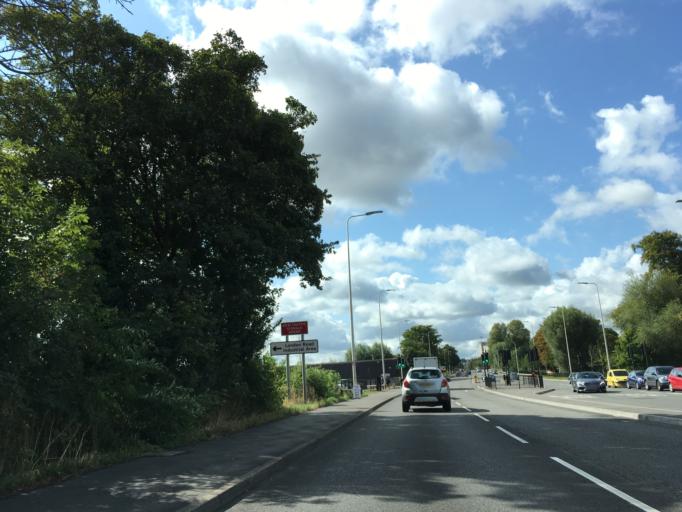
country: GB
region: England
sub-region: West Berkshire
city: Newbury
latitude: 51.4054
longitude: -1.3176
